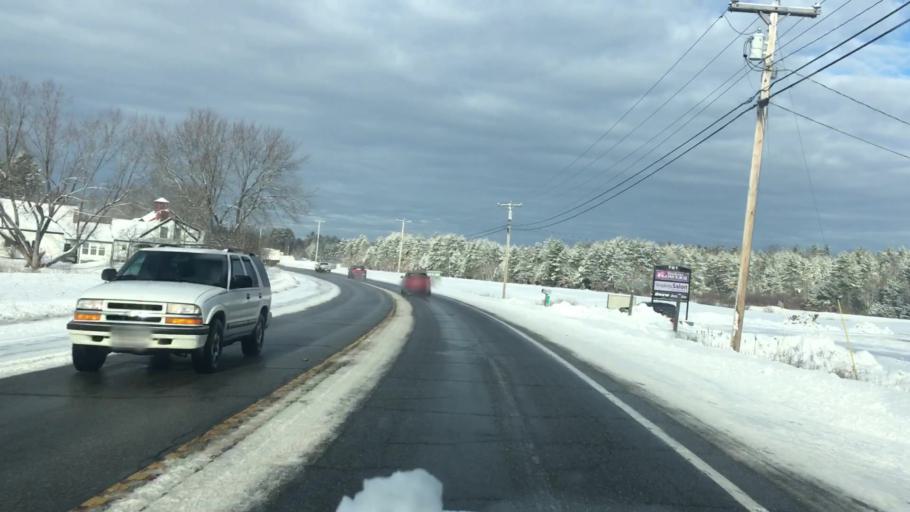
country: US
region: Maine
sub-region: Cumberland County
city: Raymond
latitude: 43.9536
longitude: -70.5543
